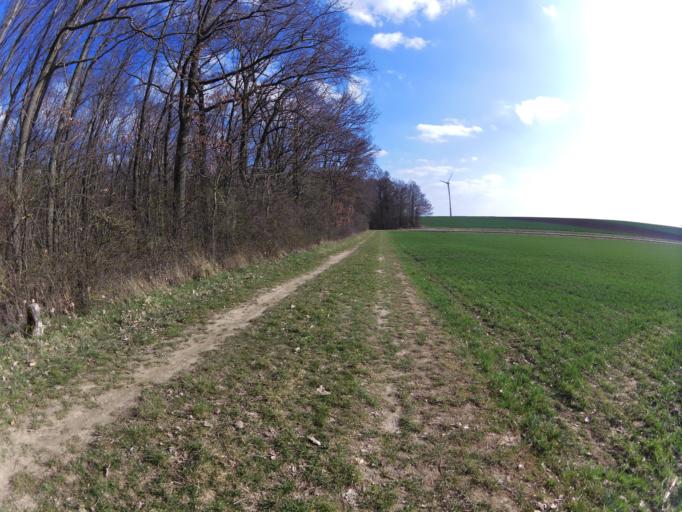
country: DE
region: Bavaria
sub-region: Regierungsbezirk Unterfranken
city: Nordheim
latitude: 49.8427
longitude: 10.1611
